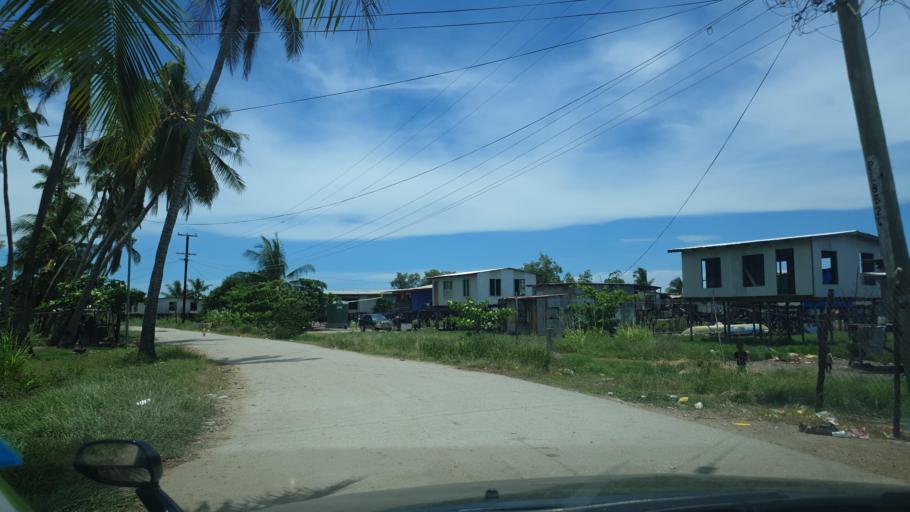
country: PG
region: National Capital
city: Port Moresby
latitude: -9.4177
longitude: 147.0434
